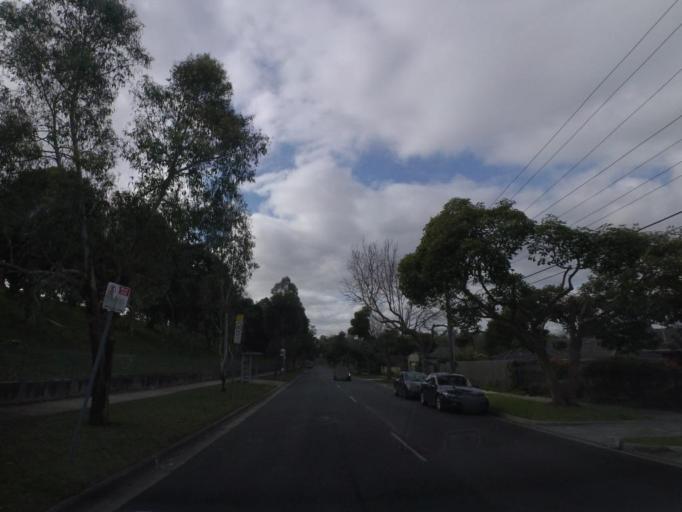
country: AU
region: Victoria
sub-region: Maroondah
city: Ringwood East
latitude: -37.8013
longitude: 145.2389
